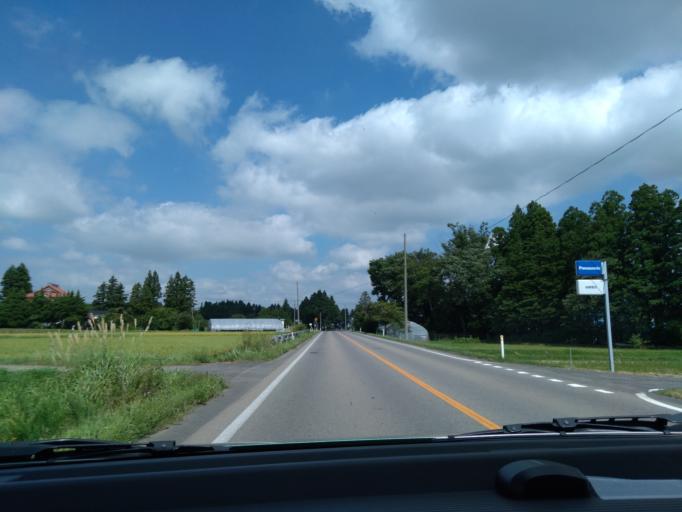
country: JP
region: Iwate
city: Hanamaki
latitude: 39.4681
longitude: 141.1027
